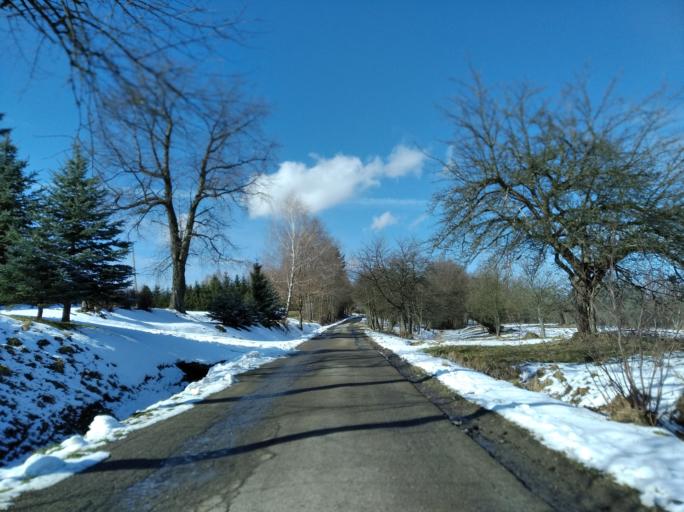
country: PL
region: Subcarpathian Voivodeship
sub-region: Powiat brzozowski
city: Jablonica Polska
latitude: 49.7286
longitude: 21.8716
